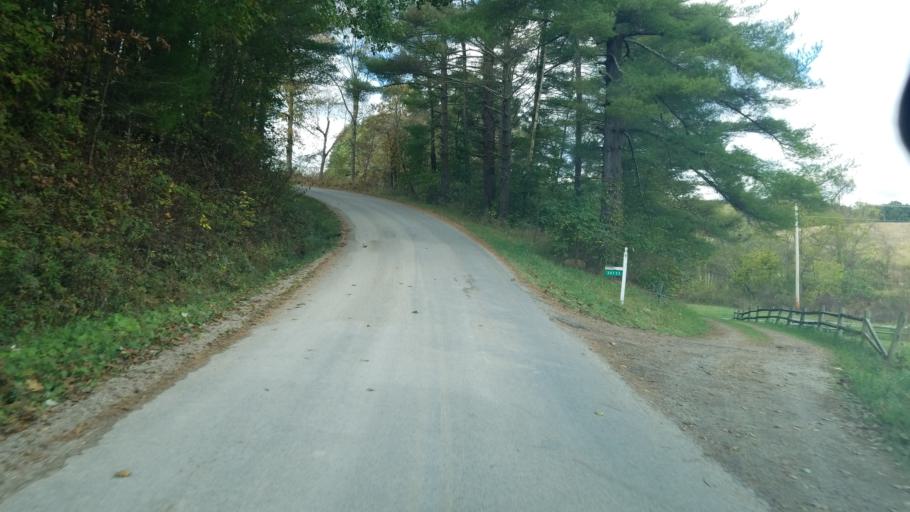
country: US
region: Ohio
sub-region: Vinton County
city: McArthur
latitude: 39.2214
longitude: -82.5167
